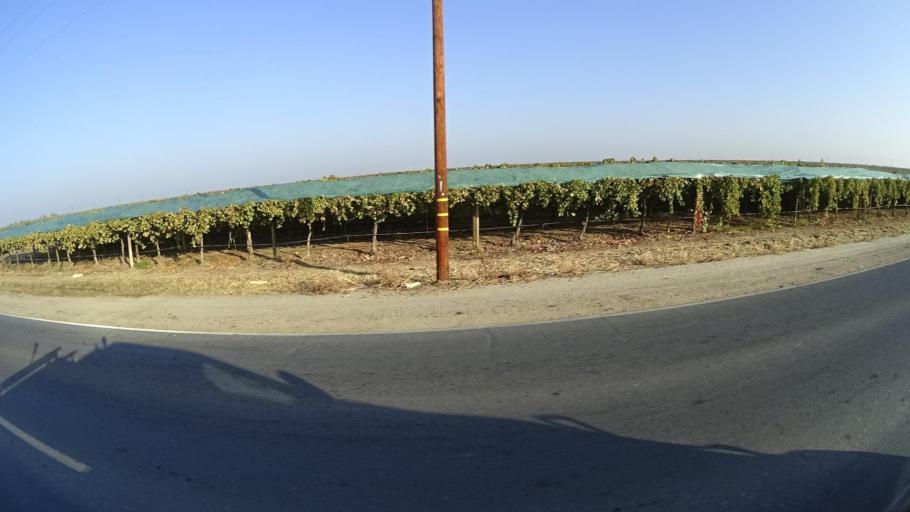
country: US
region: California
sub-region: Kern County
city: Delano
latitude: 35.7905
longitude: -119.2100
